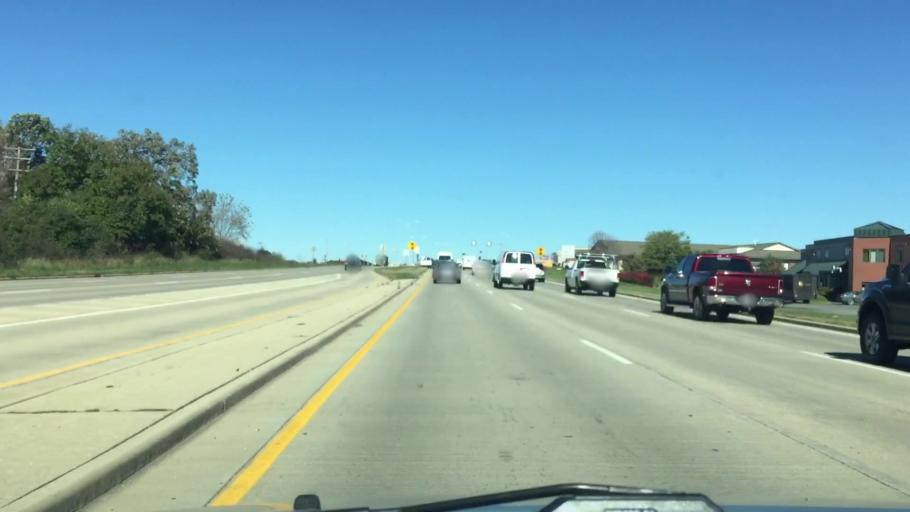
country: US
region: Wisconsin
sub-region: Waukesha County
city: Waukesha
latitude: 43.0179
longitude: -88.2008
